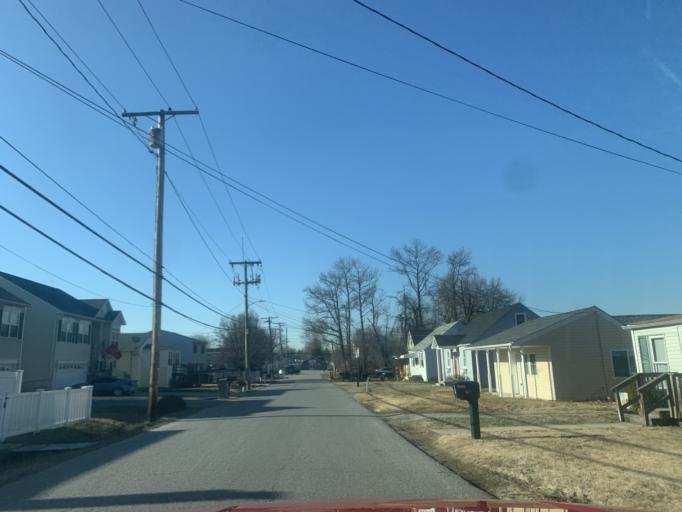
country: US
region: Maryland
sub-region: Anne Arundel County
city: Riviera Beach
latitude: 39.1687
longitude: -76.5288
